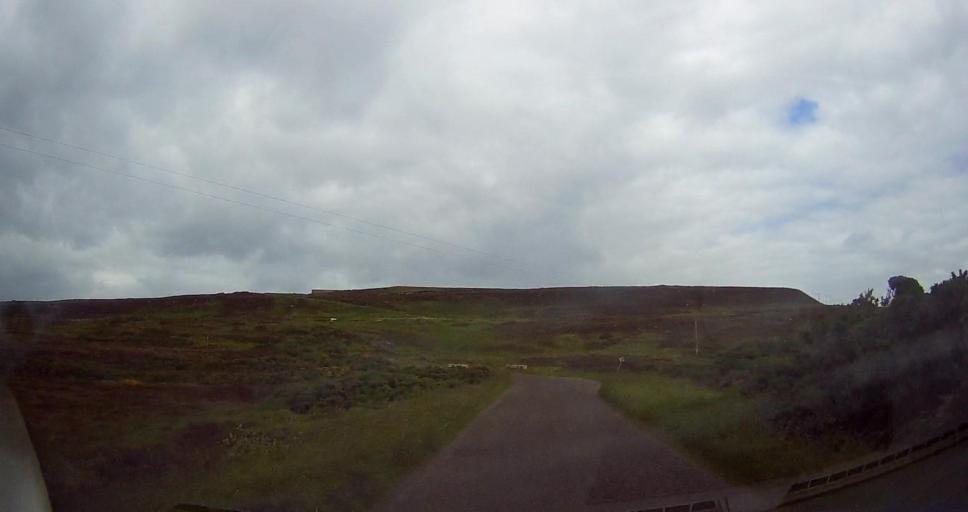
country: GB
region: Scotland
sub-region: Highland
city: Thurso
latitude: 58.6566
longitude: -3.3716
